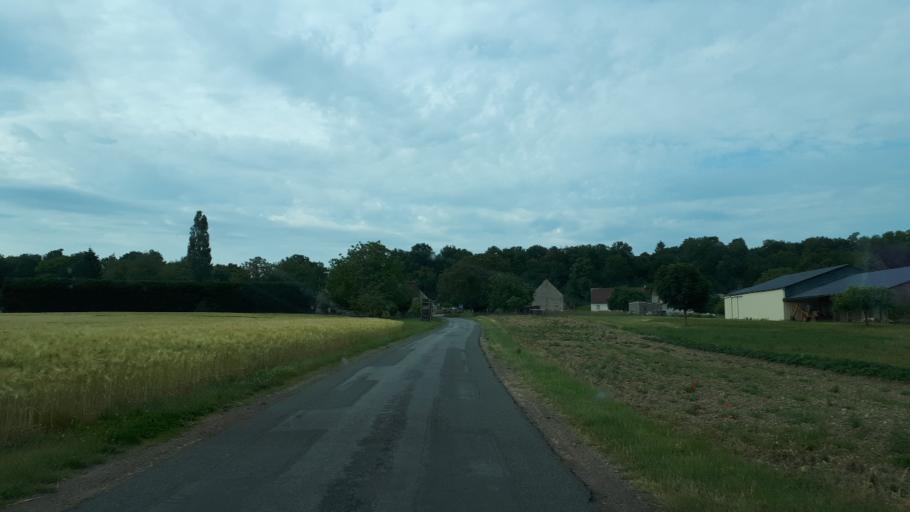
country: FR
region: Centre
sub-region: Departement du Loir-et-Cher
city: Villiers-sur-Loir
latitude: 47.7761
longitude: 1.0071
